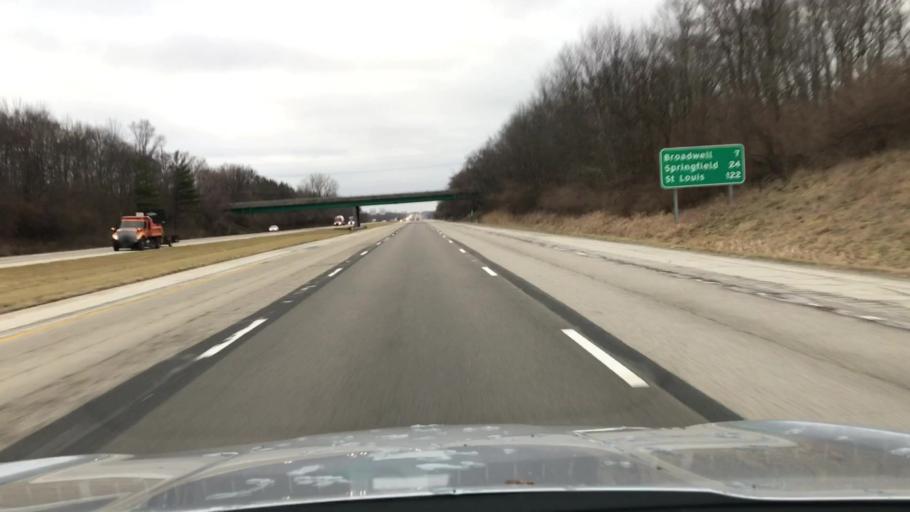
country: US
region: Illinois
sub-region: Logan County
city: Lincoln
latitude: 40.1489
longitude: -89.4175
